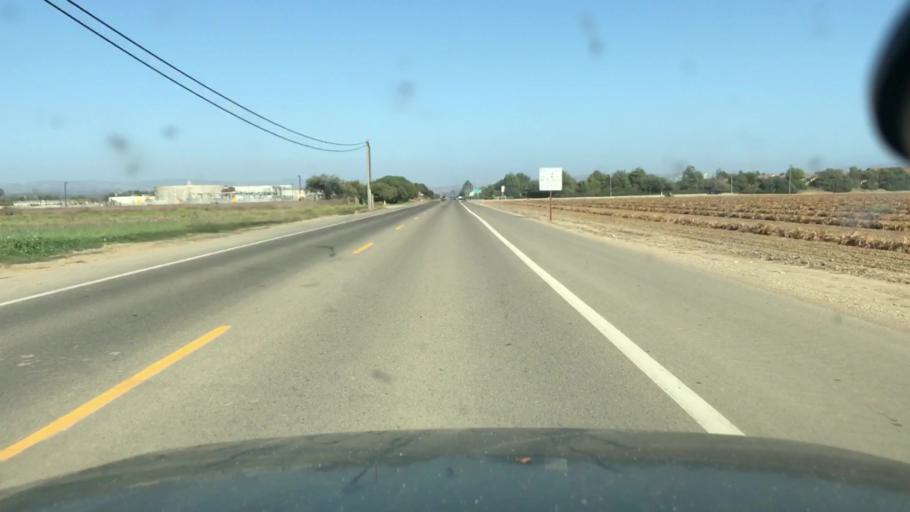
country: US
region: California
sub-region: Santa Barbara County
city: Lompoc
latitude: 34.6611
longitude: -120.4874
